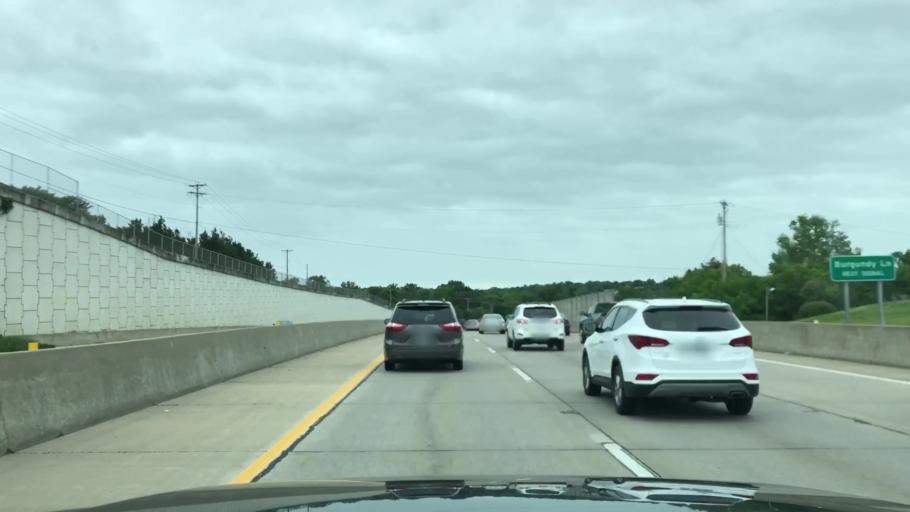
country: US
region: Missouri
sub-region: Saint Louis County
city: Manchester
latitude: 38.6018
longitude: -90.5097
